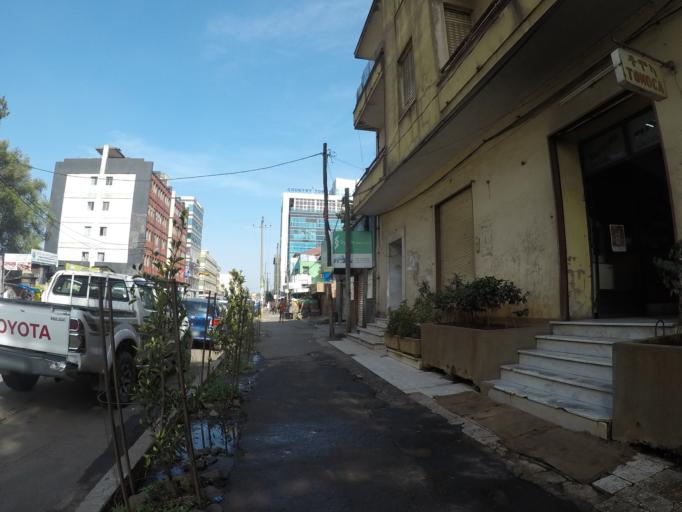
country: ET
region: Adis Abeba
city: Addis Ababa
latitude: 9.0240
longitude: 38.7515
